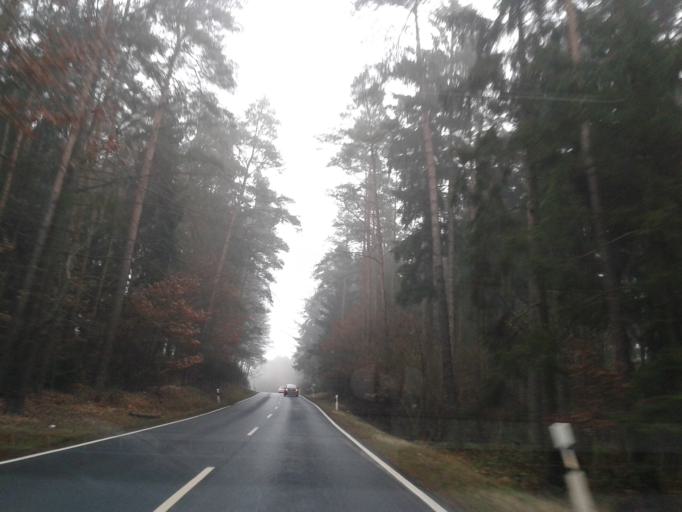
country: DE
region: Bavaria
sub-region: Upper Franconia
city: Sesslach
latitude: 50.2031
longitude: 10.7972
